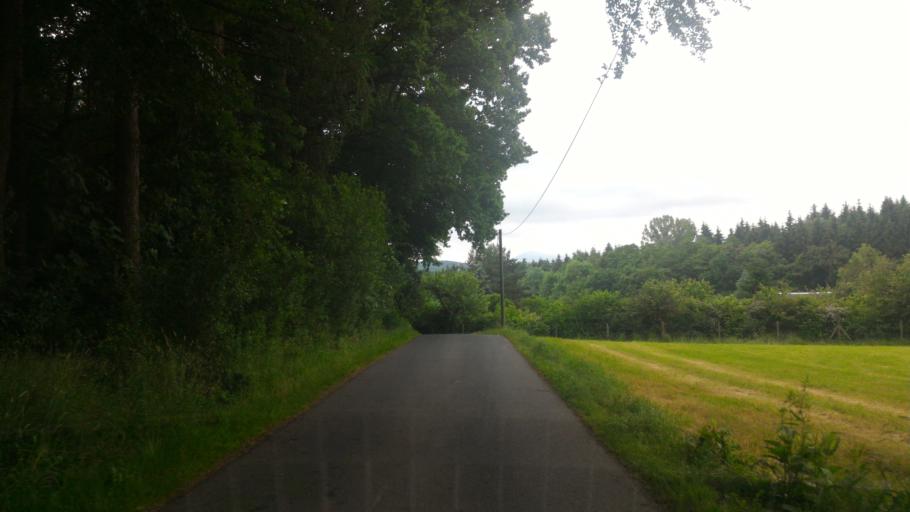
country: DE
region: Saxony
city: Neugersdorf
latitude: 50.9574
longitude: 14.6239
